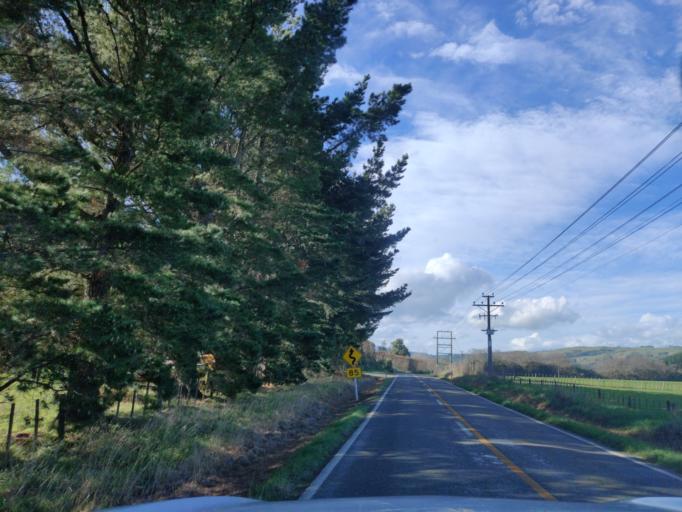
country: NZ
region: Manawatu-Wanganui
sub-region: Palmerston North City
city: Palmerston North
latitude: -40.3366
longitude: 175.7254
